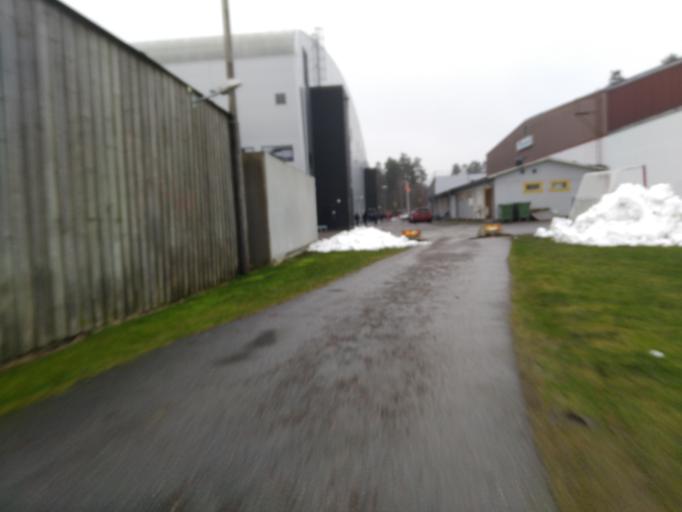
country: SE
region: Vaestra Goetaland
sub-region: Lidkopings Kommun
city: Lidkoping
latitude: 58.4954
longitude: 13.1427
